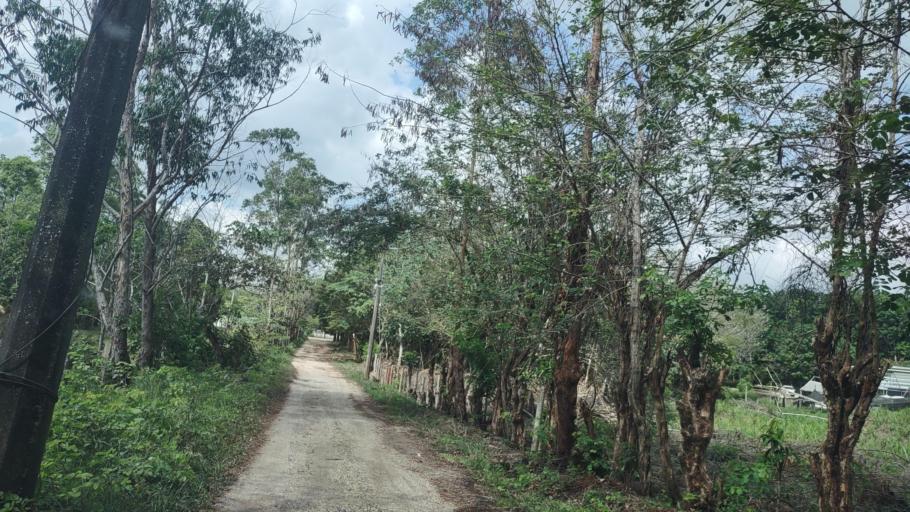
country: MX
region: Veracruz
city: Las Choapas
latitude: 17.9448
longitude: -94.1043
